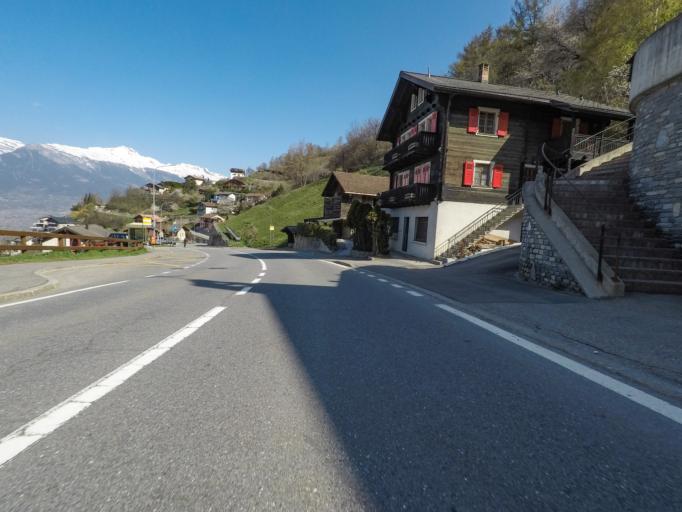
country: CH
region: Valais
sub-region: Conthey District
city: Basse-Nendaz
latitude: 46.1891
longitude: 7.3272
